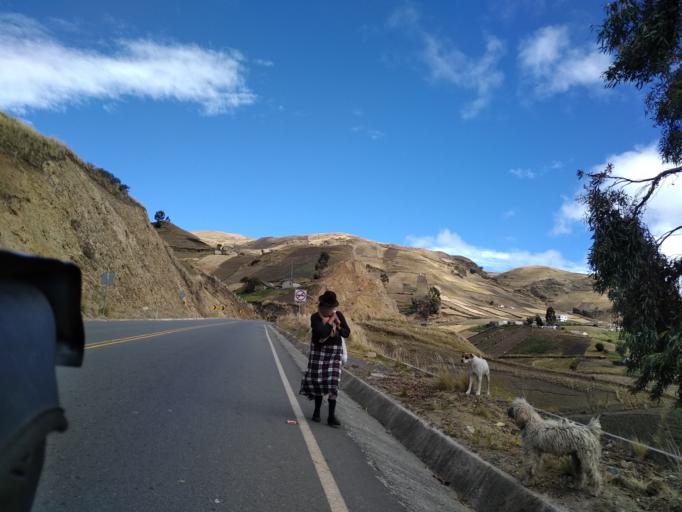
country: EC
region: Cotopaxi
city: Pujili
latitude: -0.9631
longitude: -78.9065
